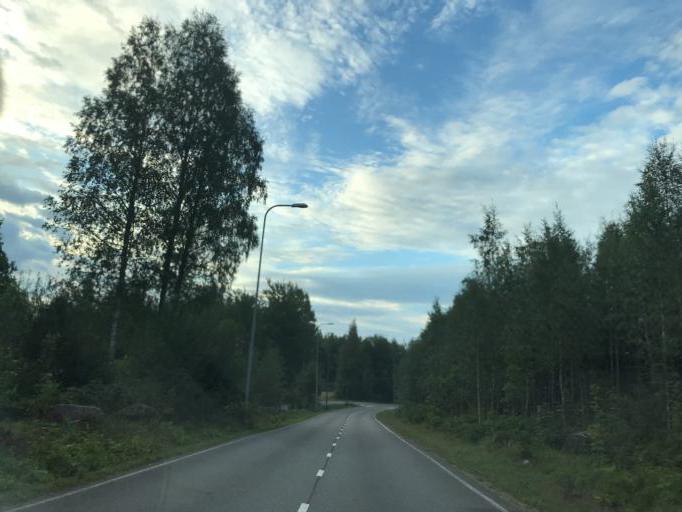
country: FI
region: Uusimaa
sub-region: Helsinki
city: Vihti
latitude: 60.4079
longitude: 24.4903
